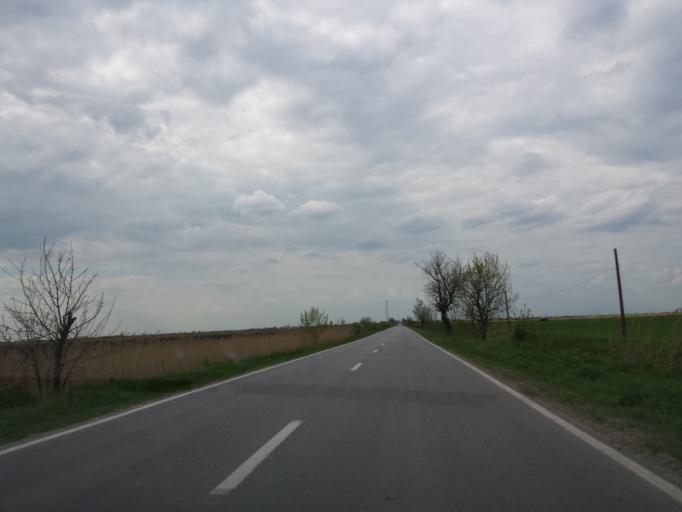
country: RO
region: Timis
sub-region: Comuna Sanpetru Mare
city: Sanpetru Mare
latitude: 46.0364
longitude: 20.6567
